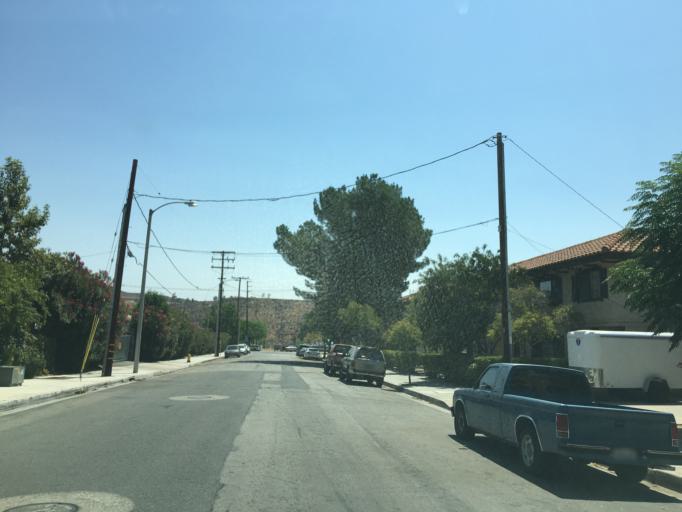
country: US
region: California
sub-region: Los Angeles County
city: Castaic
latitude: 34.4964
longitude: -118.6179
